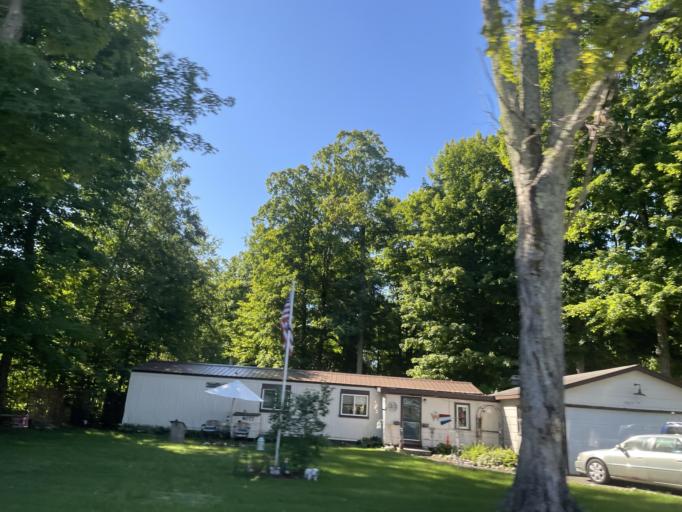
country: US
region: Michigan
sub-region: Benzie County
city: Beulah
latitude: 44.6173
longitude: -86.0573
